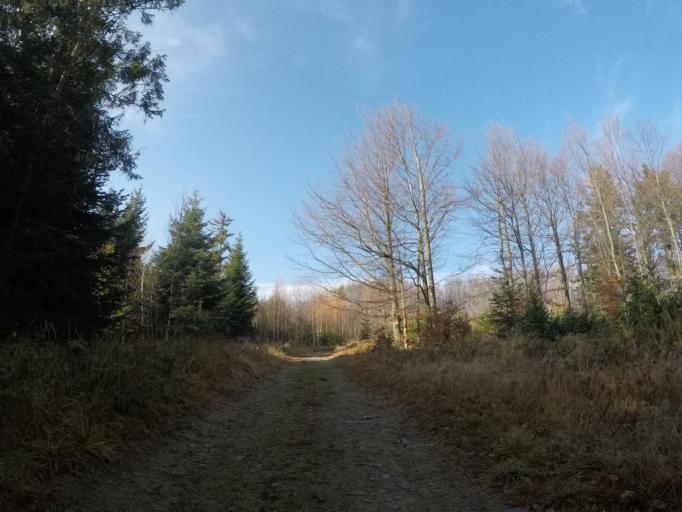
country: SK
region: Kosicky
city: Gelnica
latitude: 48.7651
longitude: 21.0628
